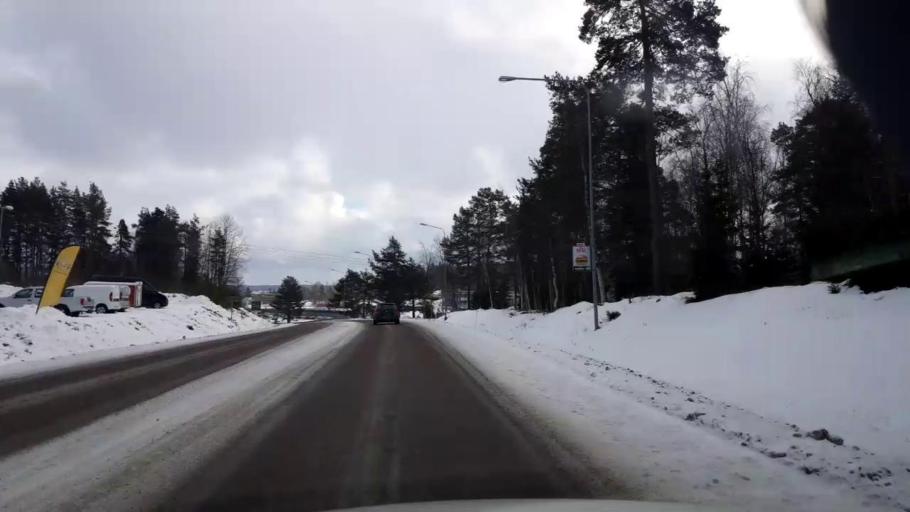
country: SE
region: Gaevleborg
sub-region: Hudiksvalls Kommun
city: Hudiksvall
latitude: 61.7375
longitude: 17.0890
